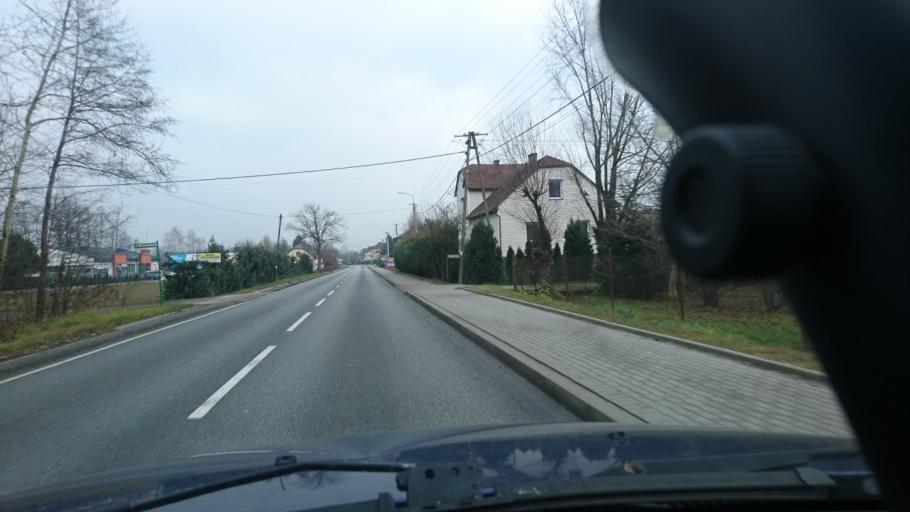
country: PL
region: Silesian Voivodeship
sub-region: Powiat bielski
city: Pisarzowice
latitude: 49.8847
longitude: 19.1404
